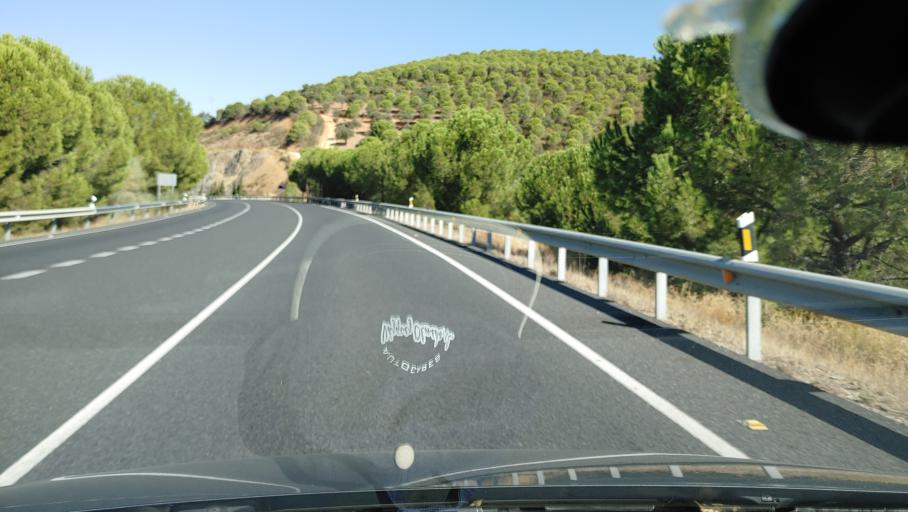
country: ES
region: Andalusia
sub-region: Province of Cordoba
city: Villaharta
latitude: 38.1096
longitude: -4.8800
